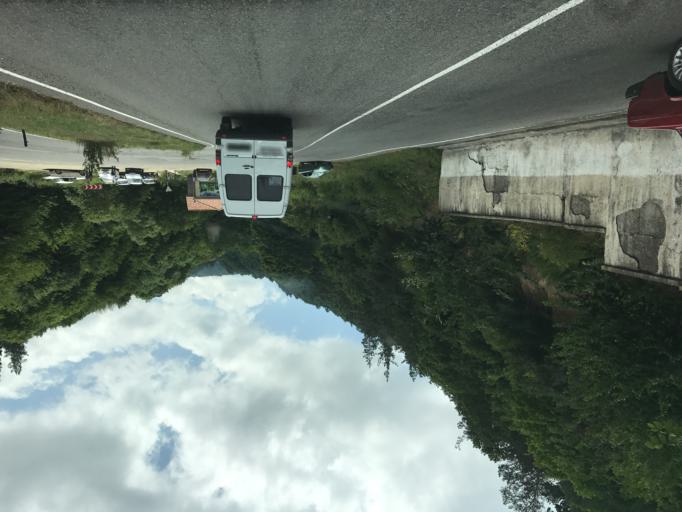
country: AM
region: Tavush
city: Dilijan
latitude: 40.6952
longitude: 44.8540
